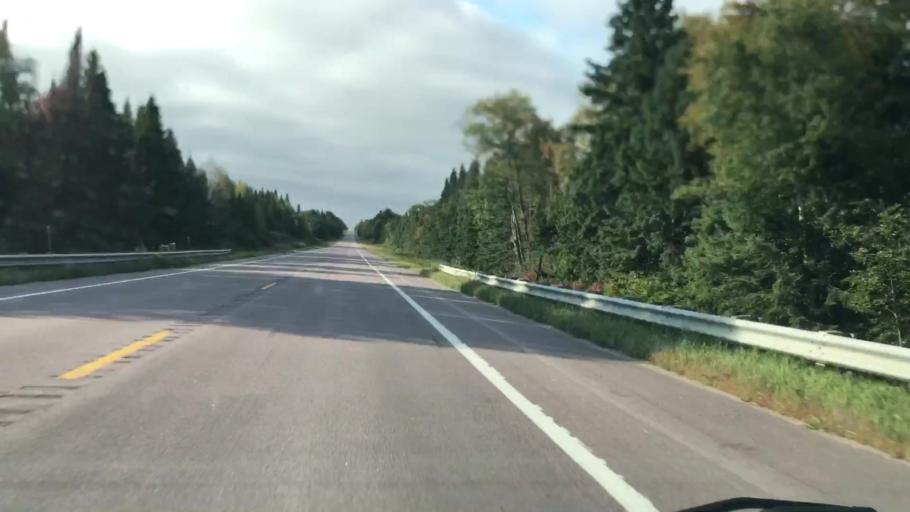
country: US
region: Michigan
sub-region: Luce County
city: Newberry
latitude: 46.3000
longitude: -85.5685
